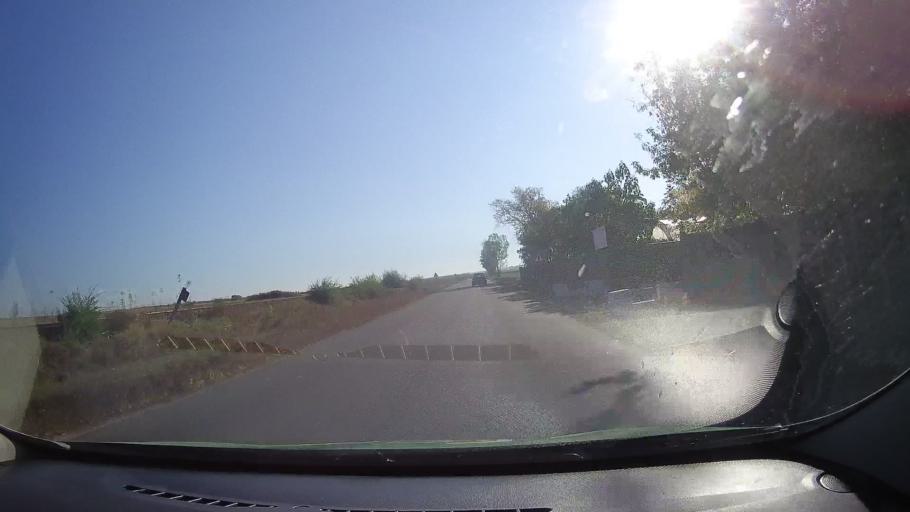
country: RO
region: Satu Mare
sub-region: Comuna Santau
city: Santau
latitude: 47.5067
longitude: 22.5280
